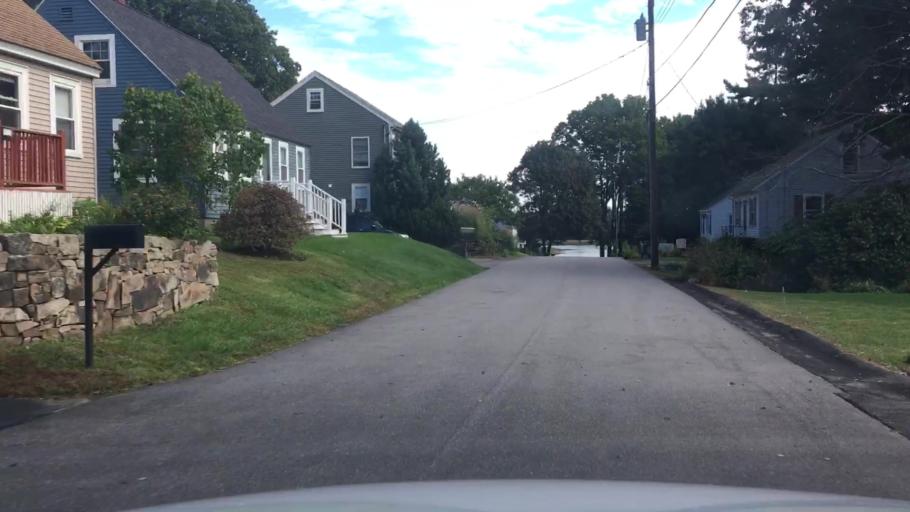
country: US
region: Maine
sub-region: York County
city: Kittery
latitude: 43.0880
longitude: -70.7276
